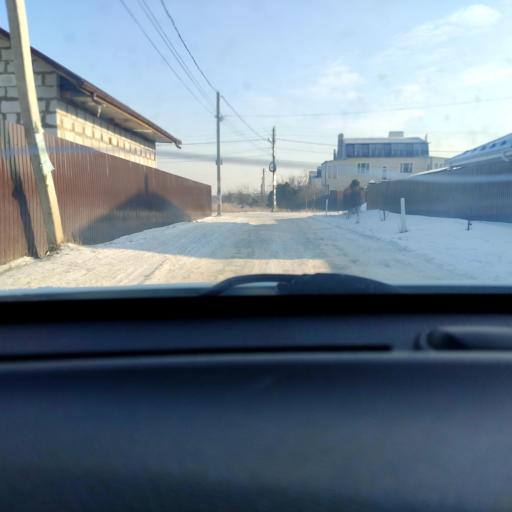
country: RU
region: Voronezj
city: Somovo
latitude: 51.6825
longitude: 39.3167
